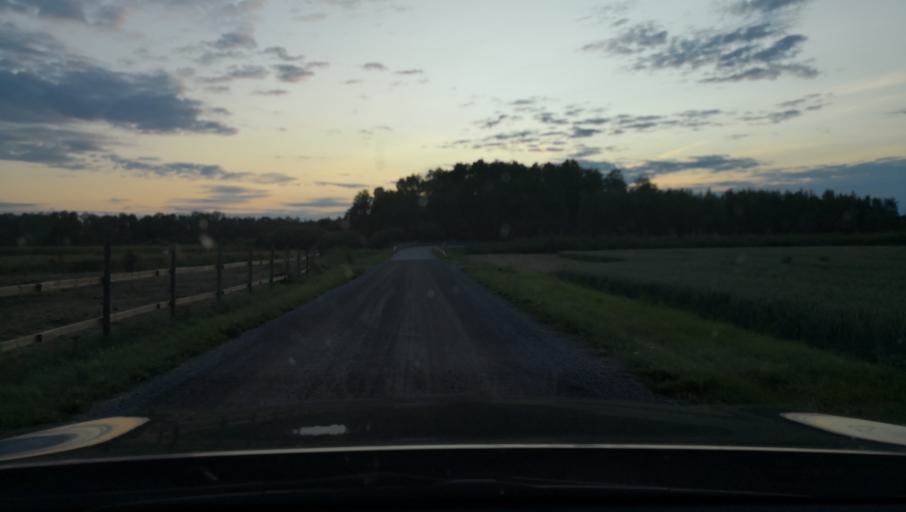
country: SE
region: Uppsala
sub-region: Osthammars Kommun
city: Bjorklinge
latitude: 60.0602
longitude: 17.5827
